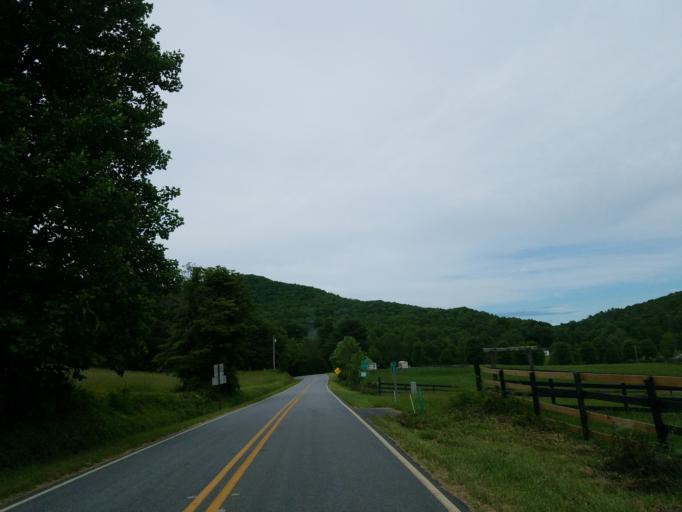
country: US
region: Georgia
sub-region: Union County
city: Blairsville
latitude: 34.7070
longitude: -83.9991
